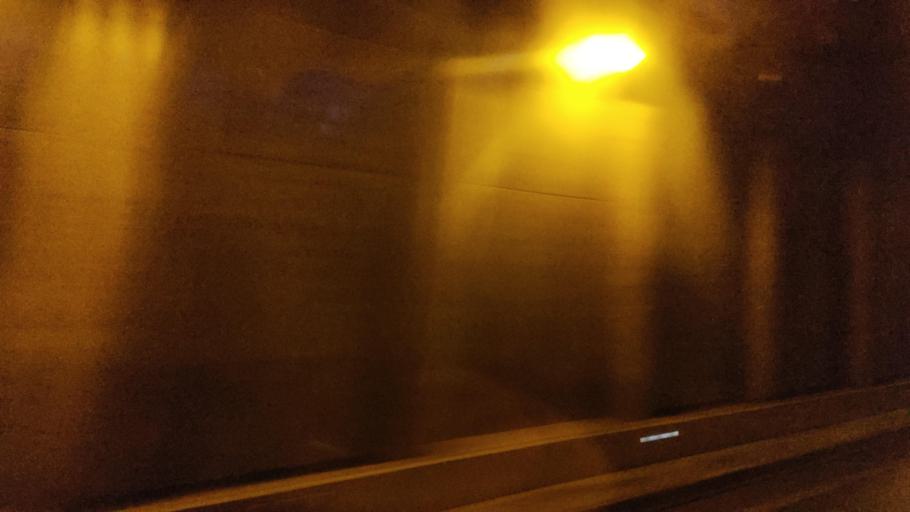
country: ES
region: Andalusia
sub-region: Provincia de Malaga
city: Benahavis
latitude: 36.4842
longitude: -4.9858
